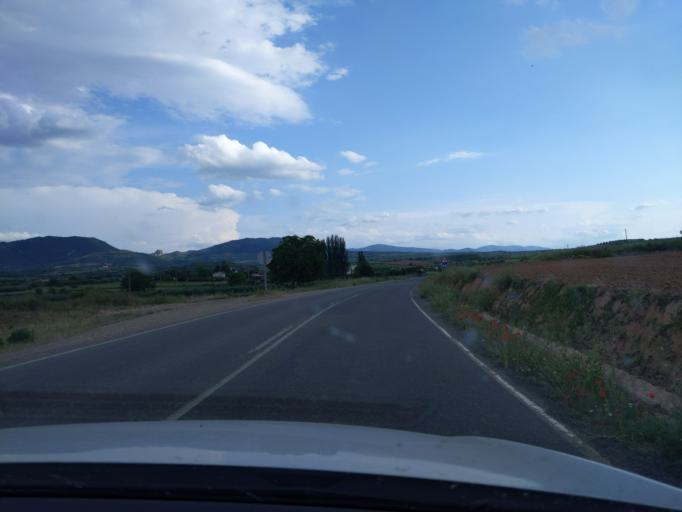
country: ES
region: La Rioja
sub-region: Provincia de La Rioja
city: Alberite
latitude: 42.4005
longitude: -2.4262
